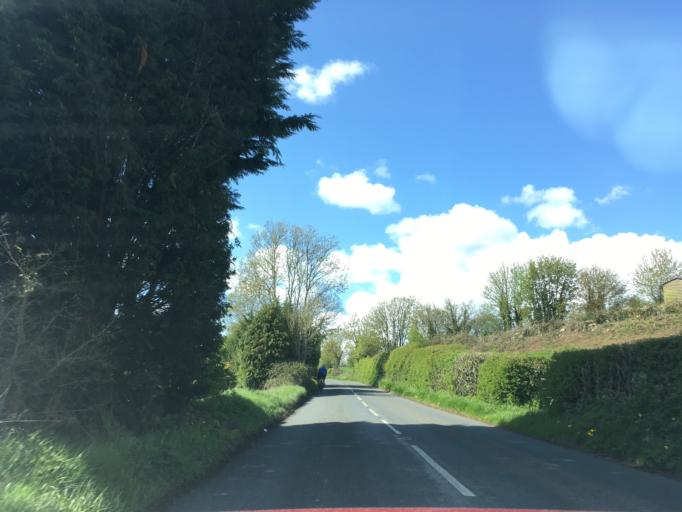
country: GB
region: England
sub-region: Gloucestershire
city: Minchinhampton
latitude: 51.6820
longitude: -2.1657
